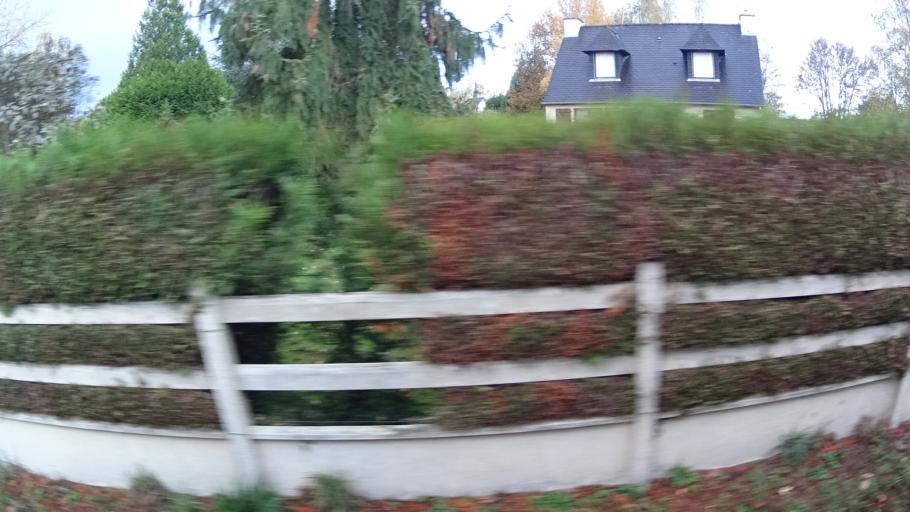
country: FR
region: Brittany
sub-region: Departement d'Ille-et-Vilaine
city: Redon
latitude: 47.6715
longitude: -2.0757
